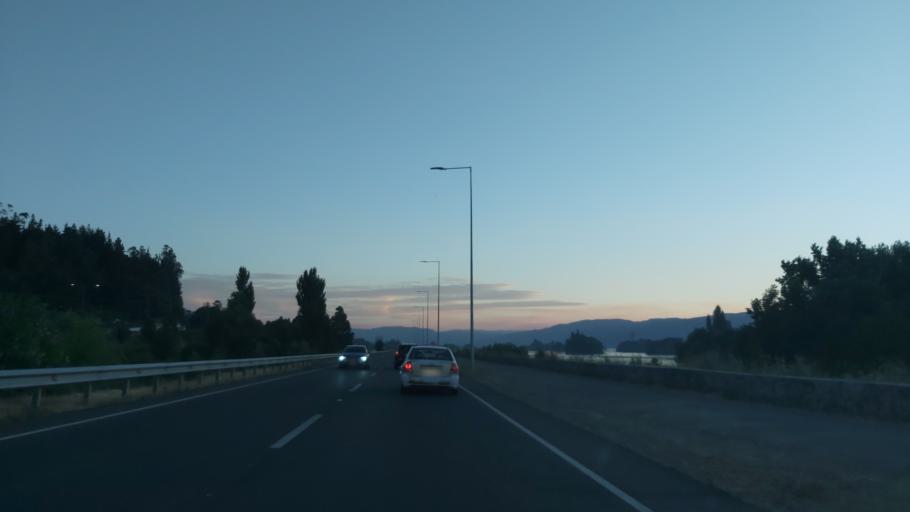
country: CL
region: Biobio
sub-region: Provincia de Concepcion
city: Chiguayante
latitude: -36.8837
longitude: -73.0386
